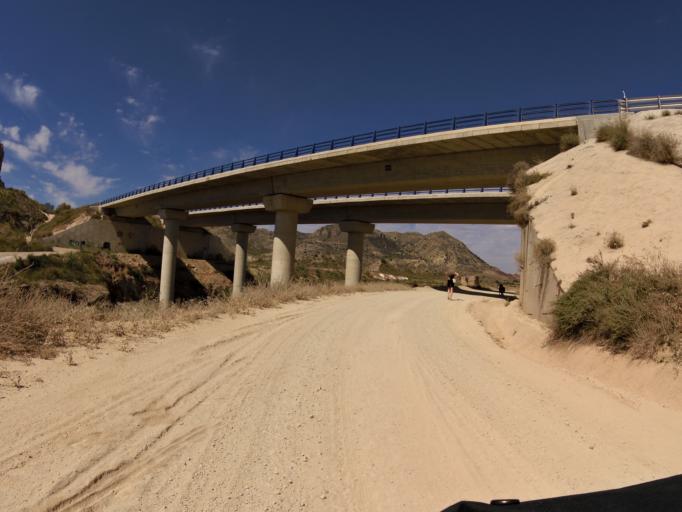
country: ES
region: Valencia
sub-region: Provincia de Alicante
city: Agost
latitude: 38.3974
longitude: -0.6092
